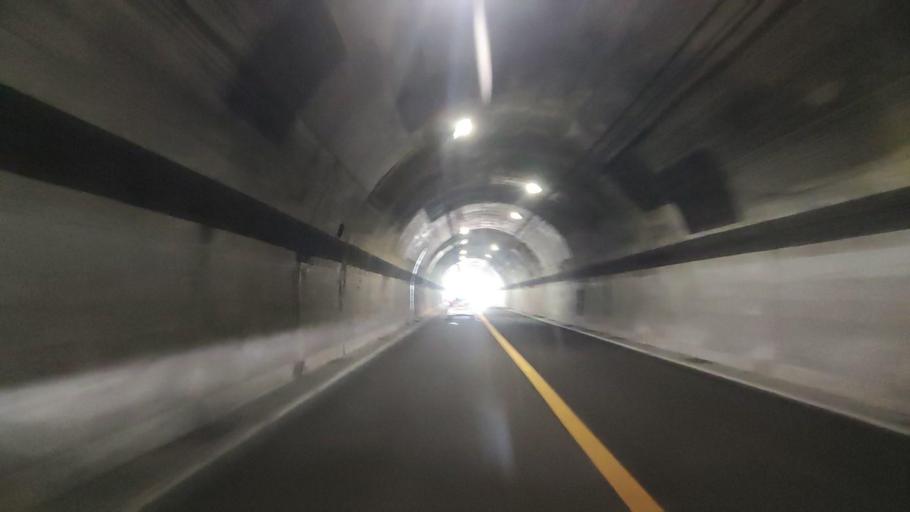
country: JP
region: Wakayama
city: Shingu
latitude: 33.5746
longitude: 135.9174
